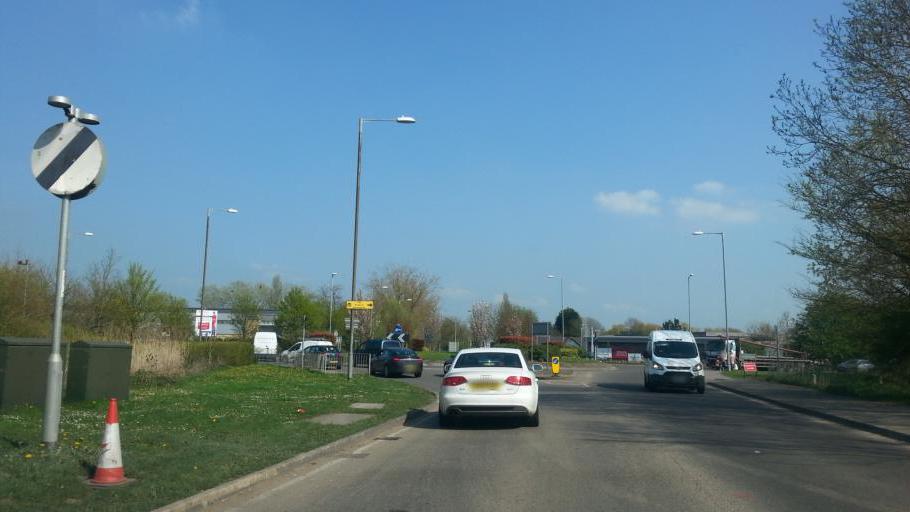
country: GB
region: England
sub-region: Cambridgeshire
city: Needingworth
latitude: 52.3315
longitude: -0.0615
